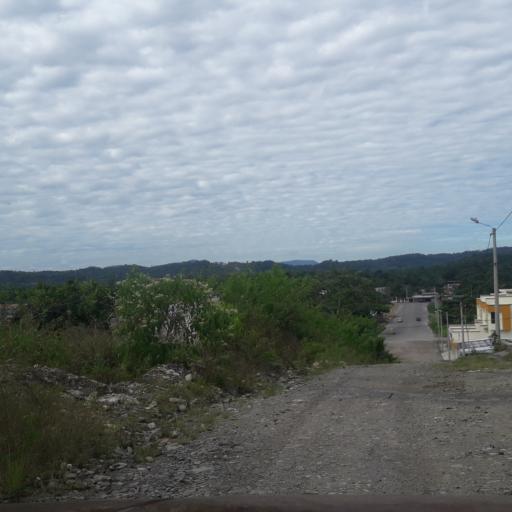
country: EC
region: Napo
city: Tena
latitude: -0.9820
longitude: -77.8235
